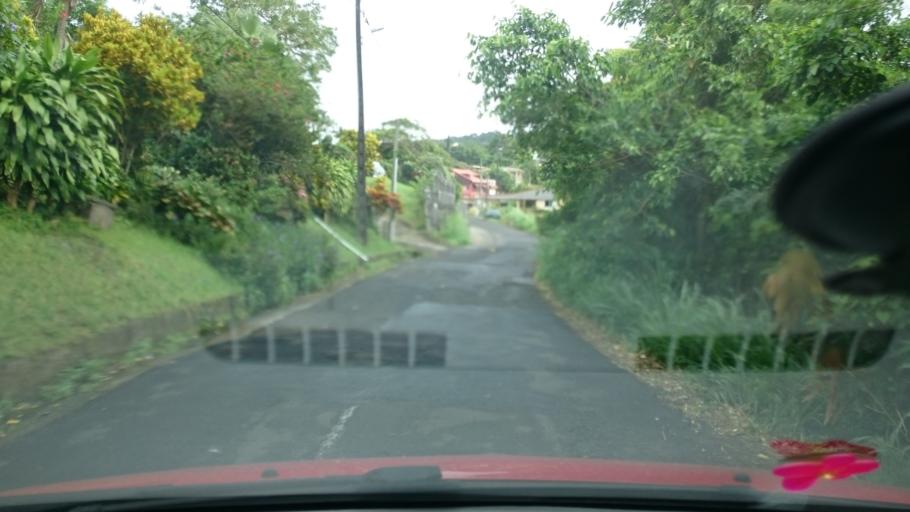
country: MQ
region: Martinique
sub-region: Martinique
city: Sainte-Luce
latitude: 14.4900
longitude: -60.9242
